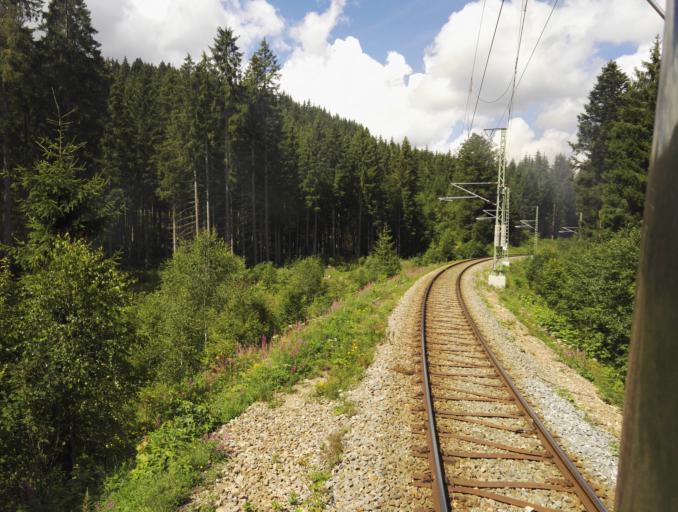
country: DE
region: Baden-Wuerttemberg
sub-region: Freiburg Region
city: Hinterzarten
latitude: 47.8547
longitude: 8.1226
